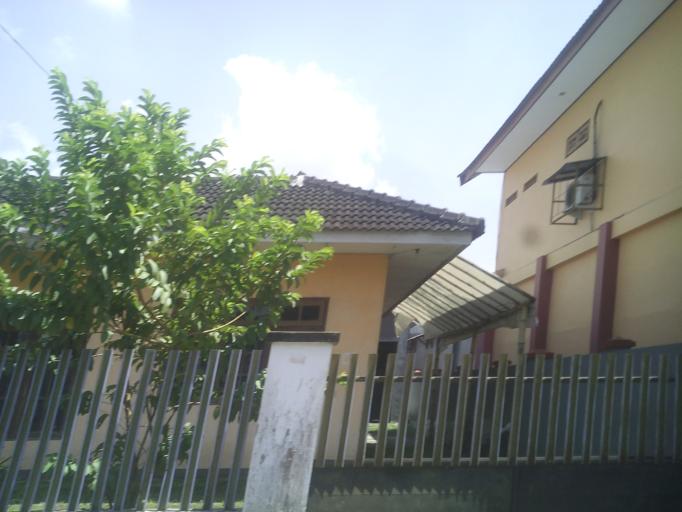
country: ID
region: East Java
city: Kloncing
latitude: -8.1911
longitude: 113.7191
